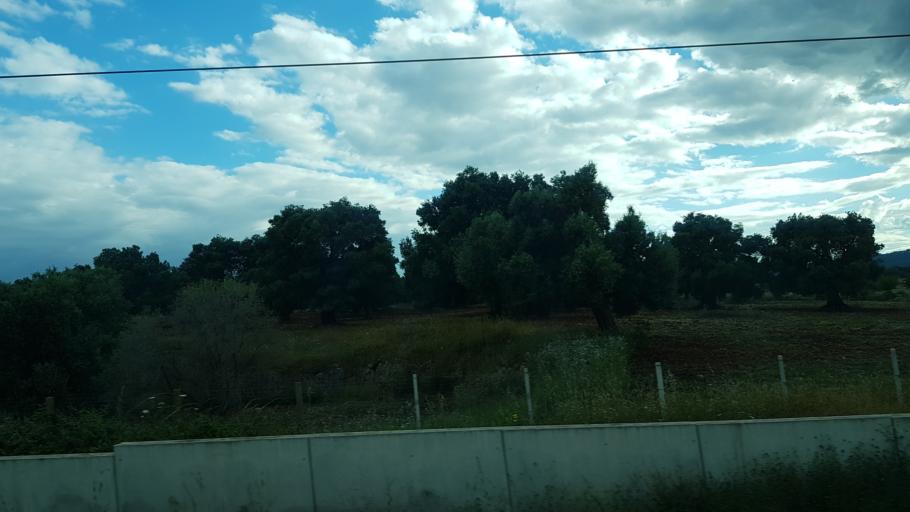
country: IT
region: Apulia
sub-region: Provincia di Brindisi
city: Pezze di Greco
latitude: 40.8435
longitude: 17.3986
